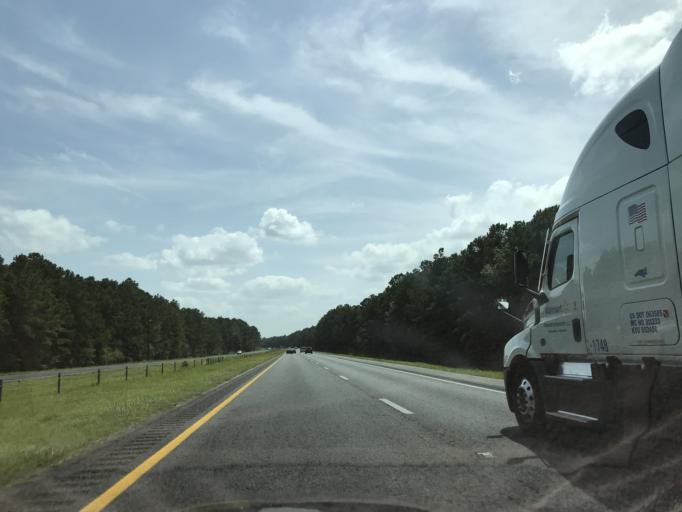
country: US
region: North Carolina
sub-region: Duplin County
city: Wallace
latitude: 34.7146
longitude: -77.9456
